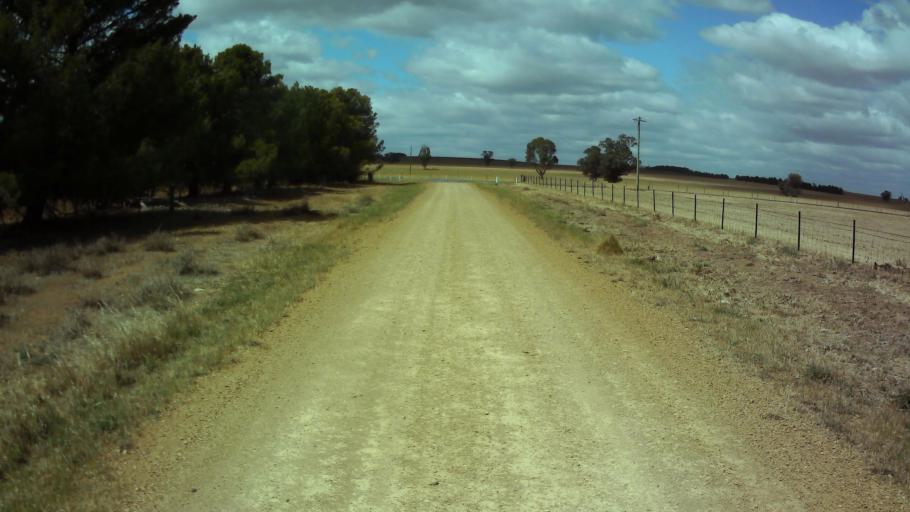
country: AU
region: New South Wales
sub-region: Weddin
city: Grenfell
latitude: -34.0662
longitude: 148.3291
